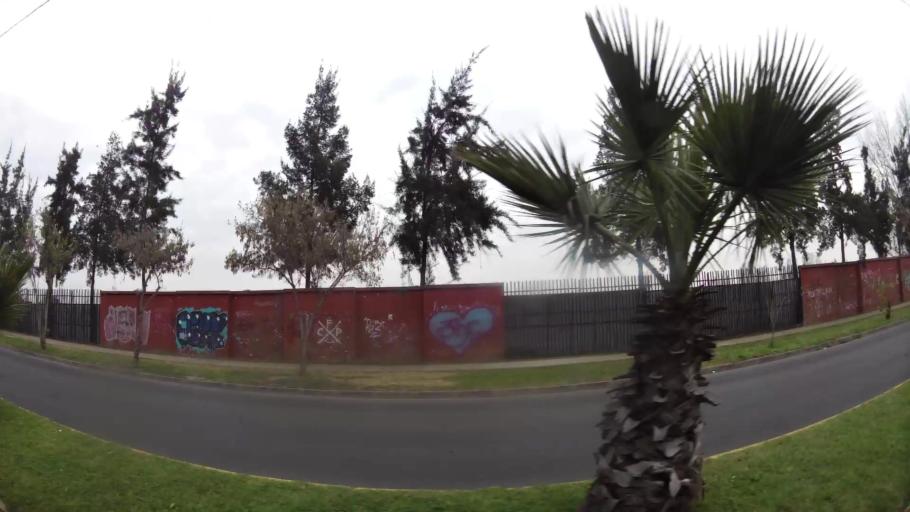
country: CL
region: Santiago Metropolitan
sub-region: Provincia de Santiago
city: Villa Presidente Frei, Nunoa, Santiago, Chile
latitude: -33.5035
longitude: -70.6033
